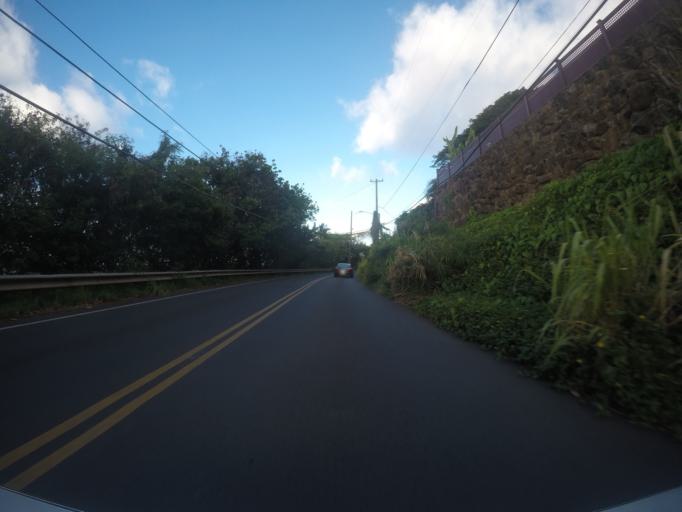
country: US
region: Hawaii
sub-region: Honolulu County
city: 'Ahuimanu
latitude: 21.4563
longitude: -157.8280
